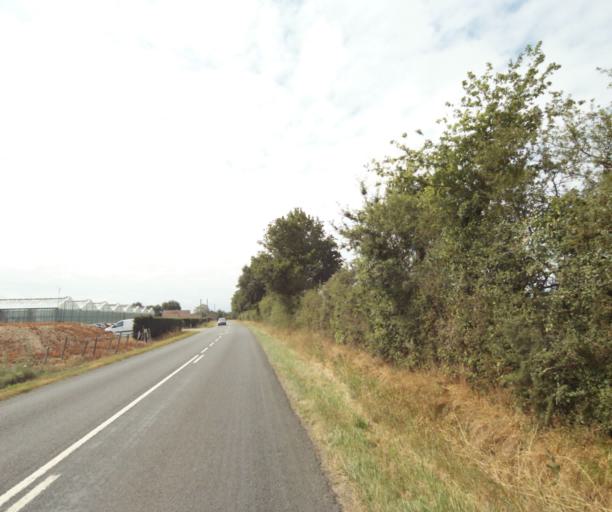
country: FR
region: Pays de la Loire
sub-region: Departement de la Sarthe
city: Sable-sur-Sarthe
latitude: 47.8142
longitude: -0.3184
